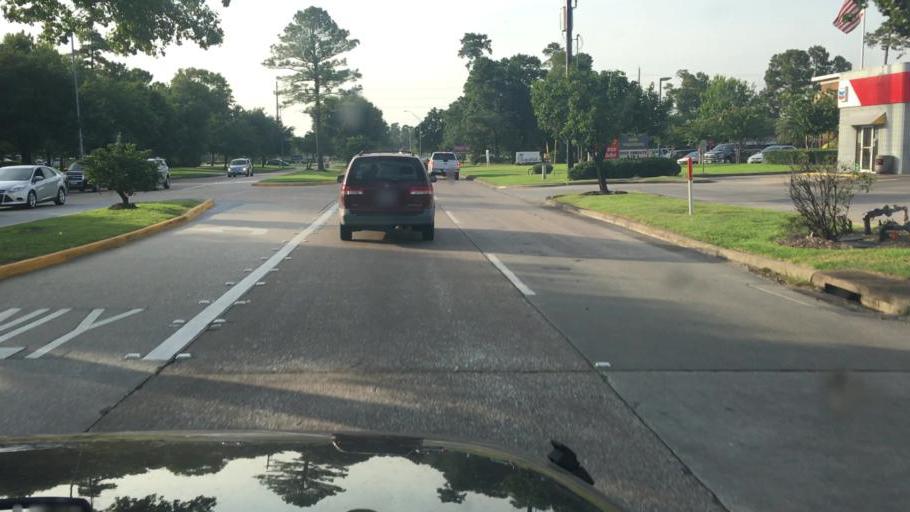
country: US
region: Texas
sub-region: Harris County
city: Atascocita
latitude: 29.9992
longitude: -95.1624
